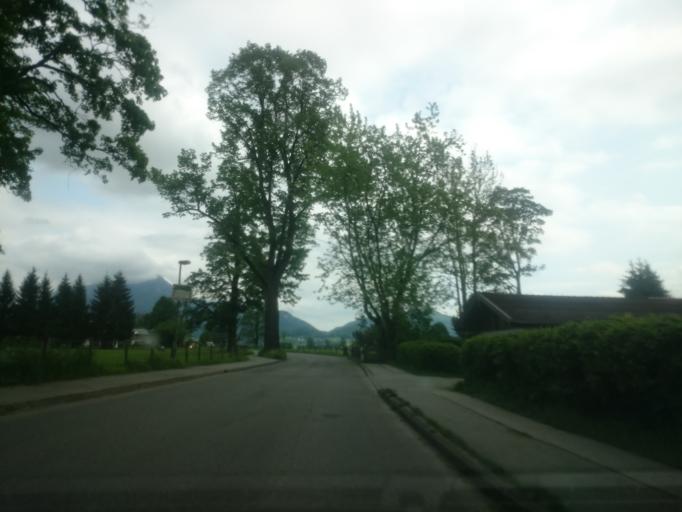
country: DE
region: Bavaria
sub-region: Upper Bavaria
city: Schoenau am Koenigssee
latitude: 47.6049
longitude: 12.9739
